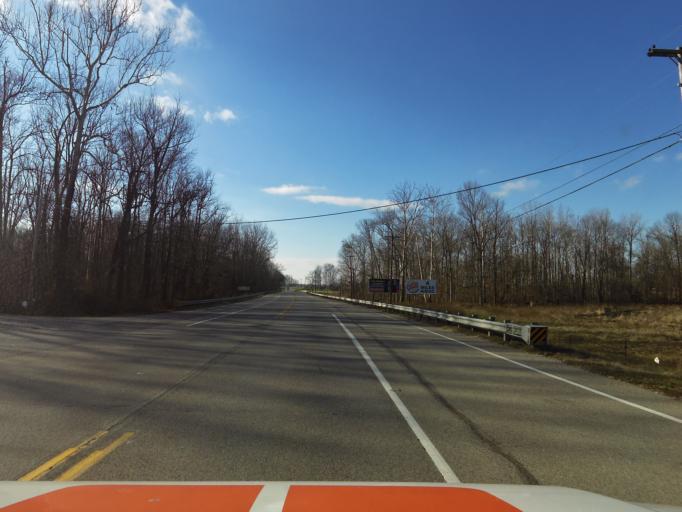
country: US
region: Indiana
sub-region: Jackson County
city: Seymour
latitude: 38.9669
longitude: -85.7957
